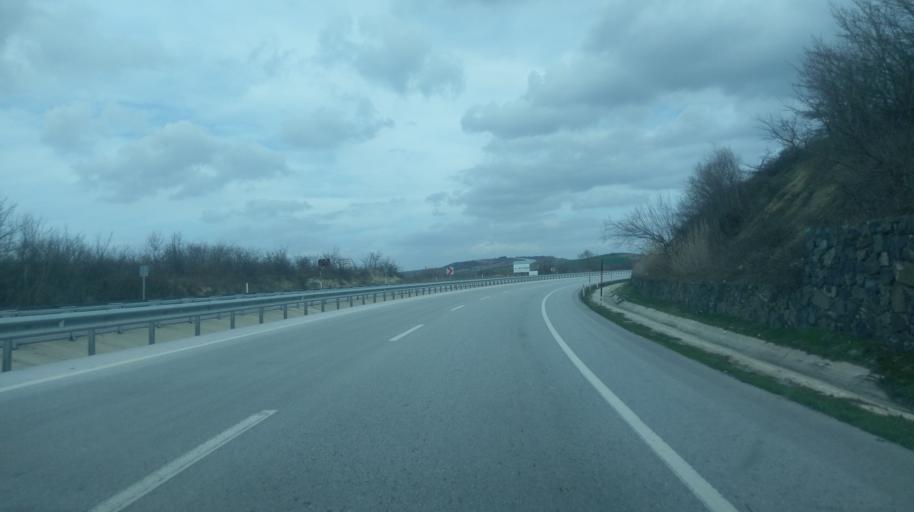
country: TR
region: Edirne
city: Uzun Keupru
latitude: 41.3024
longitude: 26.7007
